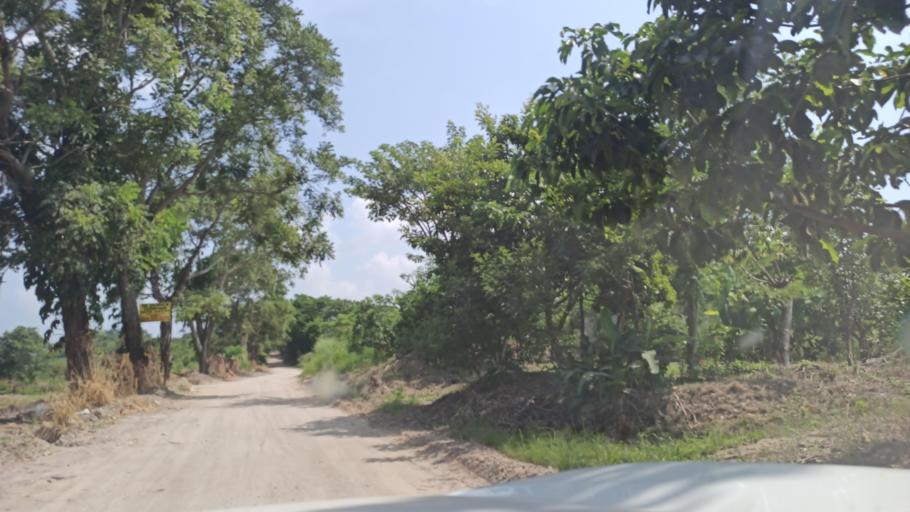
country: MX
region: Veracruz
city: Martinez de la Torre
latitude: 20.0820
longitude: -97.0787
